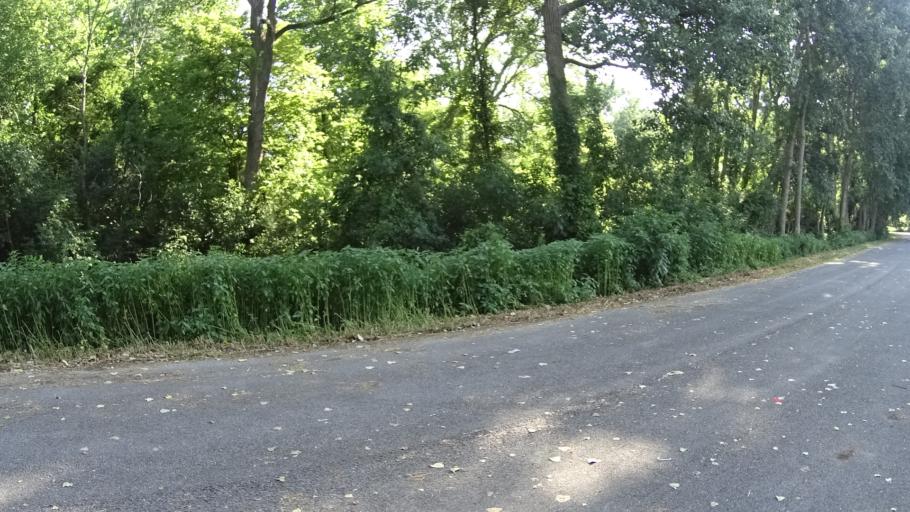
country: US
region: Ohio
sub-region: Erie County
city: Sandusky
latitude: 41.4215
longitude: -82.8234
